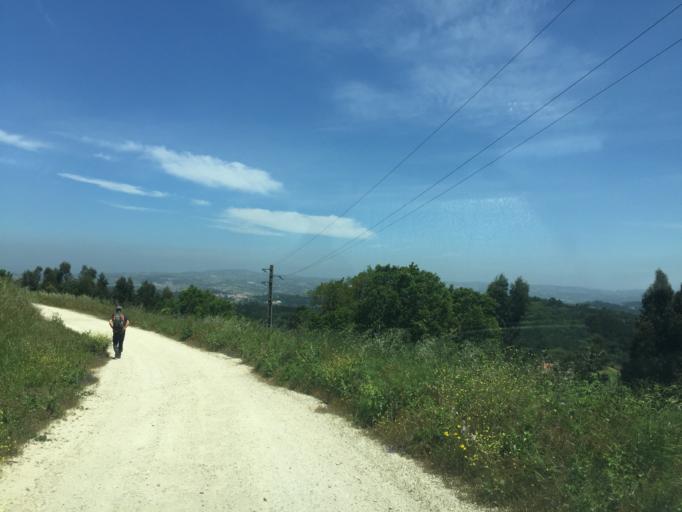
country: PT
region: Lisbon
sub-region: Mafra
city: Venda do Pinheiro
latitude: 38.8952
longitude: -9.2360
